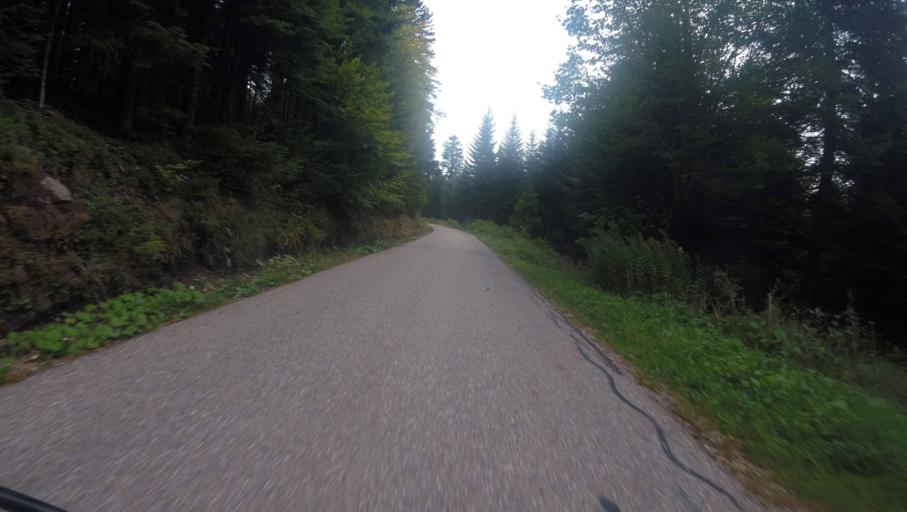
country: DE
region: Baden-Wuerttemberg
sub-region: Karlsruhe Region
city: Loffenau
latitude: 48.7606
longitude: 8.4203
